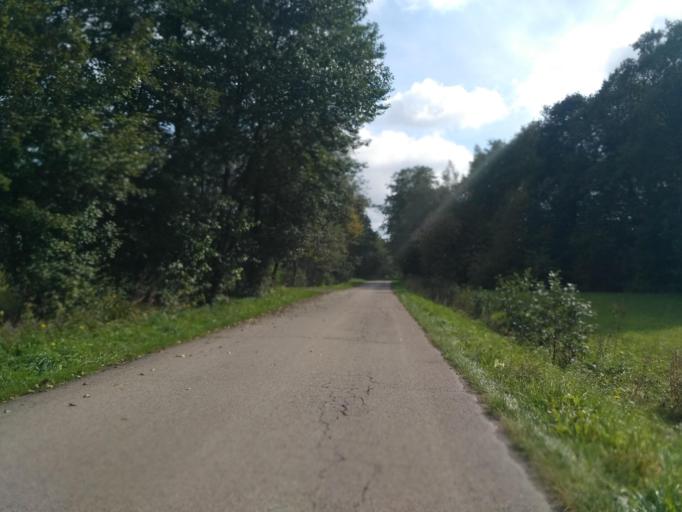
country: PL
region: Subcarpathian Voivodeship
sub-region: Powiat ropczycko-sedziszowski
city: Niedzwiada
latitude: 49.9376
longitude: 21.5298
